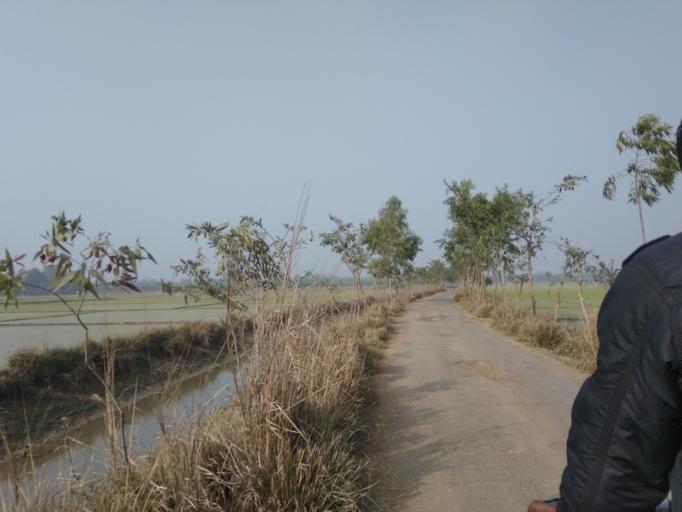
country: BD
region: Rajshahi
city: Bogra
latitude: 24.4694
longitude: 89.2679
